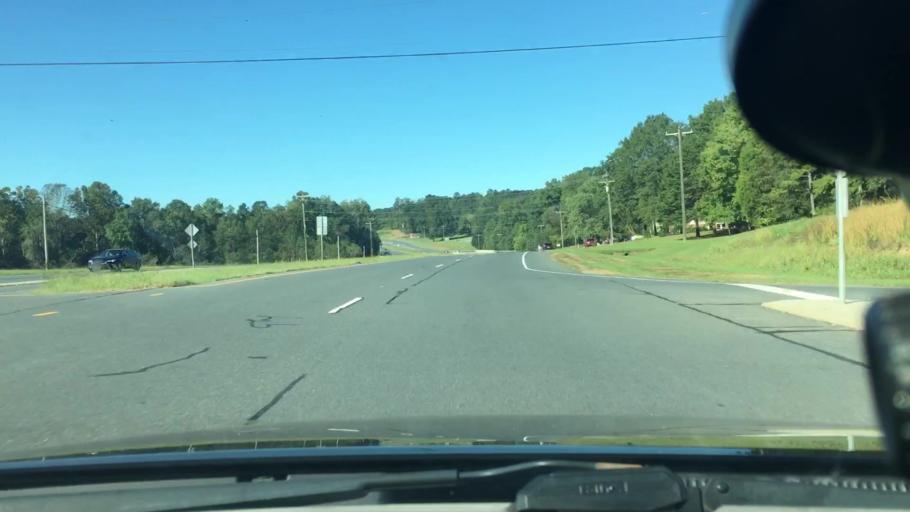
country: US
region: North Carolina
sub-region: Stanly County
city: Oakboro
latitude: 35.2725
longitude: -80.3197
